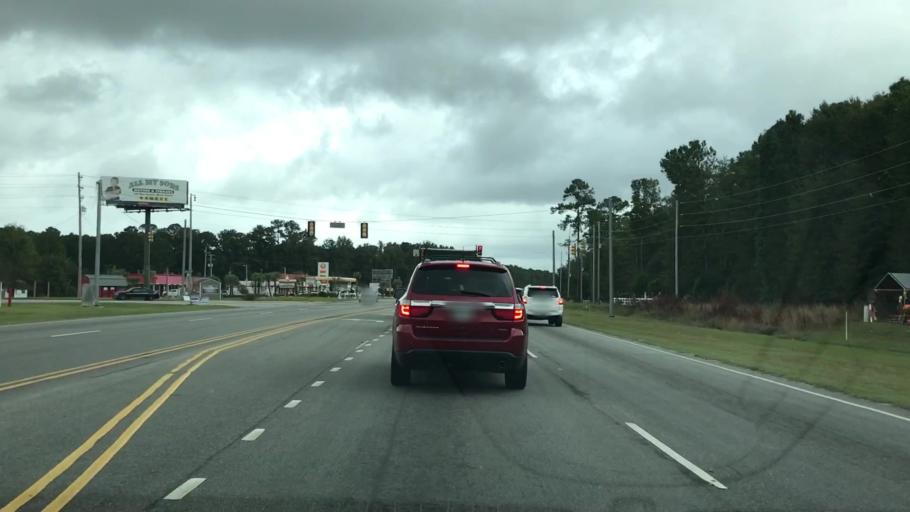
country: US
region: South Carolina
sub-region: Beaufort County
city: Bluffton
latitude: 32.3393
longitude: -80.9284
